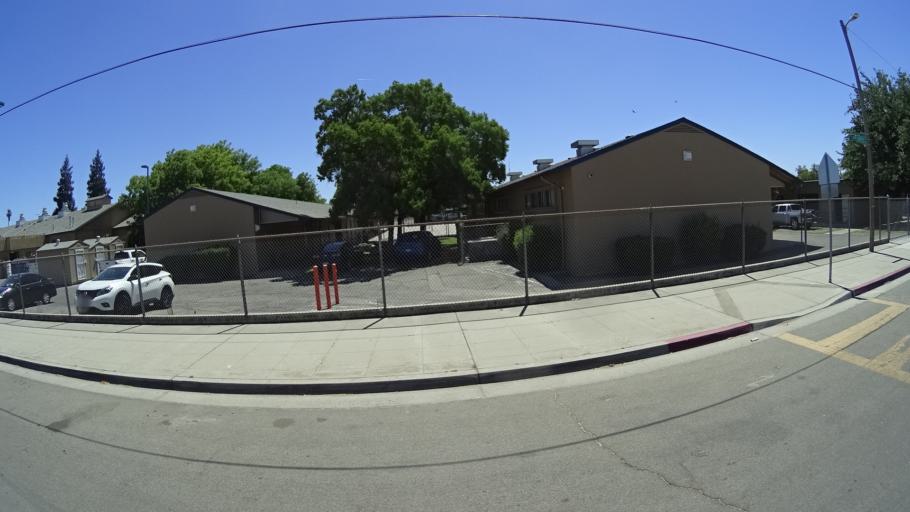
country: US
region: California
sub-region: Fresno County
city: West Park
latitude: 36.7639
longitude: -119.8378
